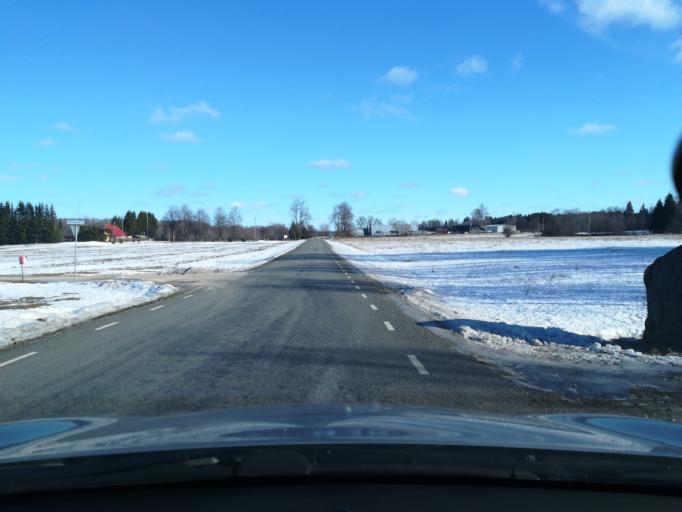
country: EE
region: Harju
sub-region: Kiili vald
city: Kiili
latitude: 59.2676
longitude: 24.7848
